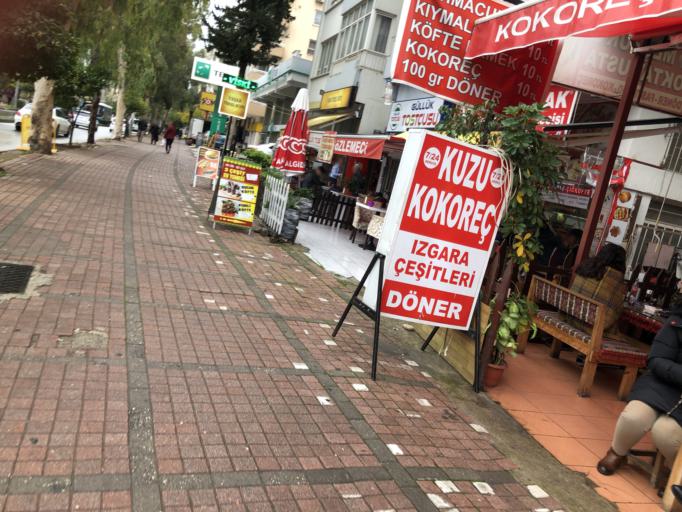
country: TR
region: Antalya
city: Antalya
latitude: 36.8944
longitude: 30.6926
